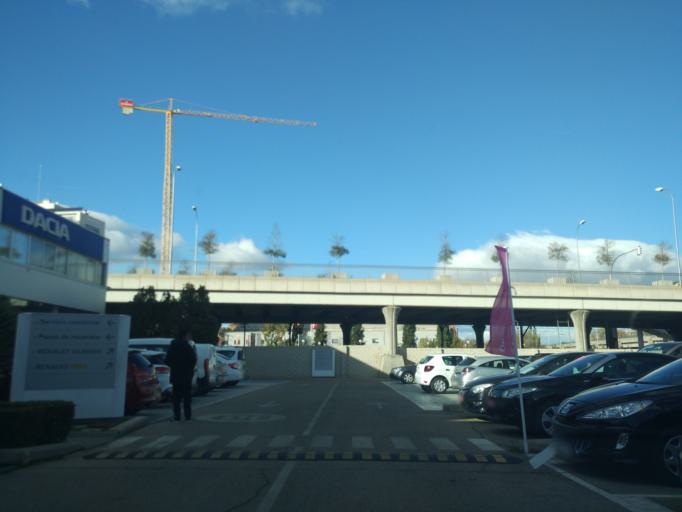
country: ES
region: Madrid
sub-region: Provincia de Madrid
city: Villaverde
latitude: 40.3451
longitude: -3.6938
